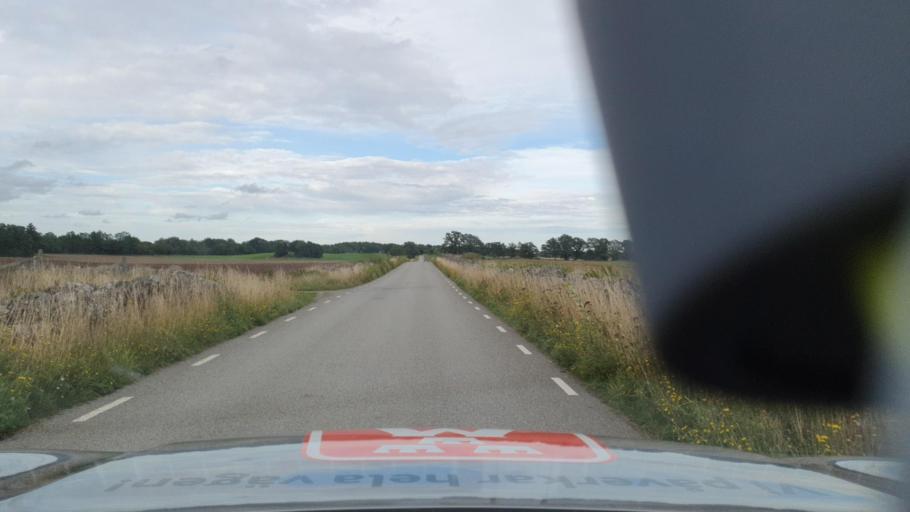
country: SE
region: Kalmar
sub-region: Kalmar Kommun
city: Lindsdal
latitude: 56.7773
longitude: 16.2637
